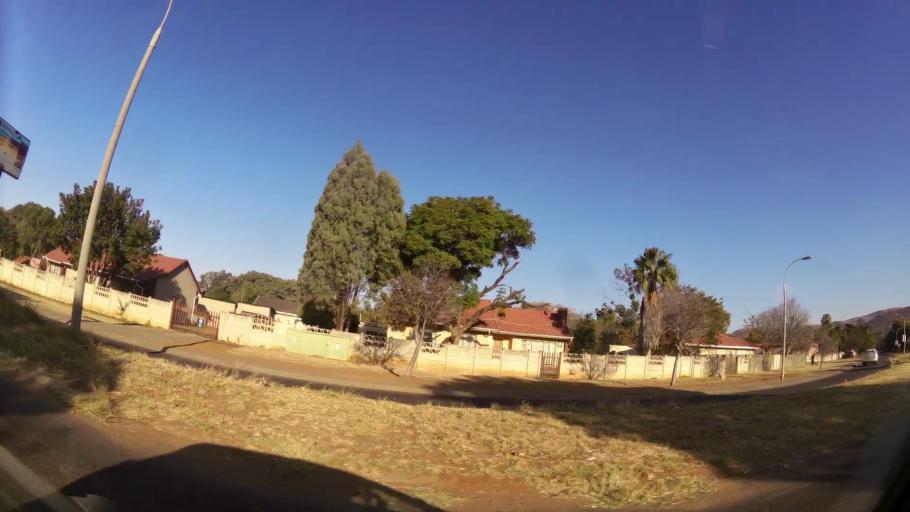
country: ZA
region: North-West
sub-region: Bojanala Platinum District Municipality
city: Rustenburg
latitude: -25.6833
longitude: 27.2178
